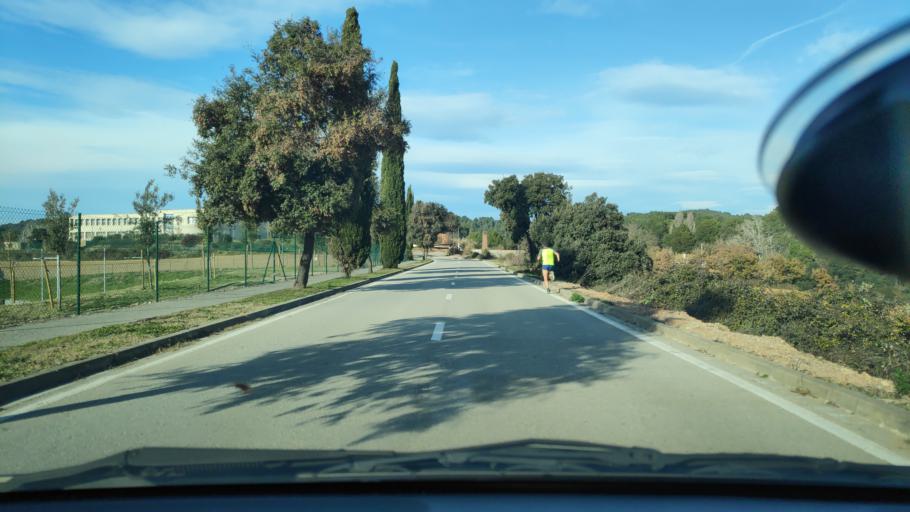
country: ES
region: Catalonia
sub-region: Provincia de Barcelona
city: Rubi
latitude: 41.4950
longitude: 2.0651
